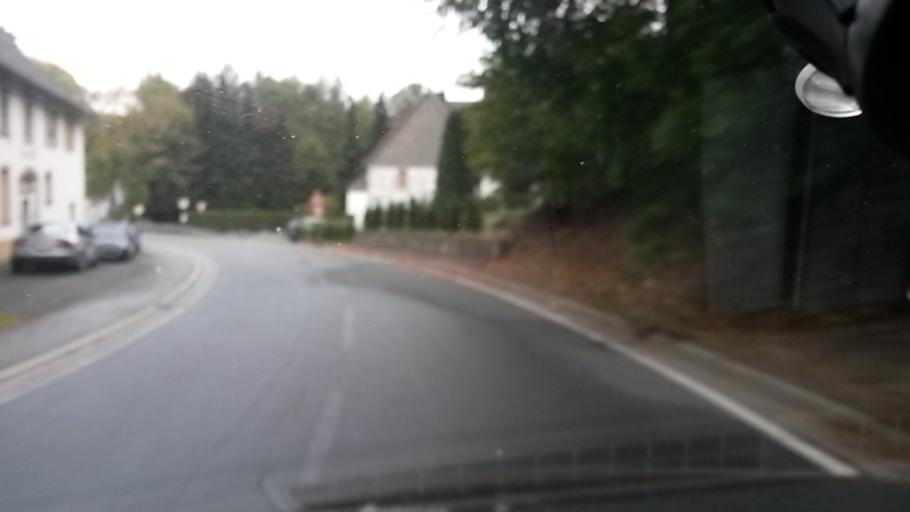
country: DE
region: North Rhine-Westphalia
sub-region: Regierungsbezirk Arnsberg
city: Herscheid
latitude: 51.1866
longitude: 7.7171
